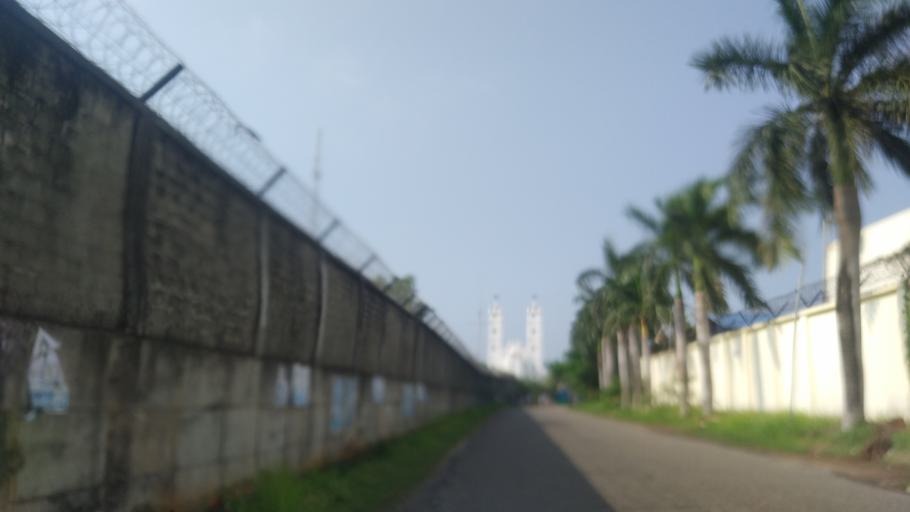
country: IN
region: Kerala
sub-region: Ernakulam
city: Cochin
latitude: 9.9870
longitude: 76.2501
